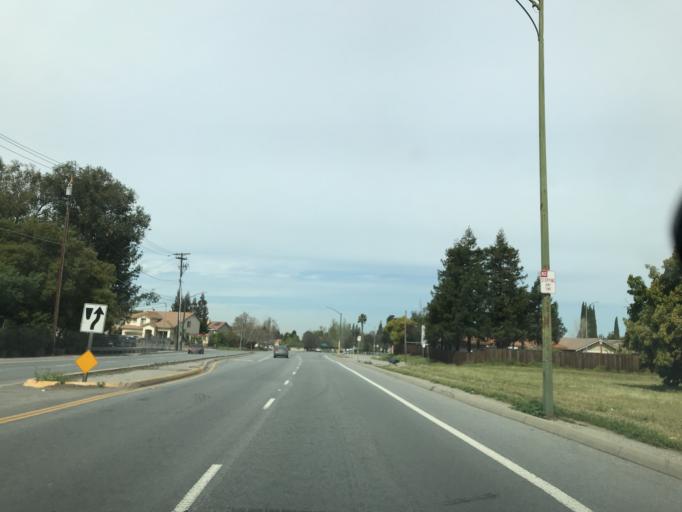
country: US
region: California
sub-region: Santa Clara County
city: Seven Trees
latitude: 37.3112
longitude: -121.7869
